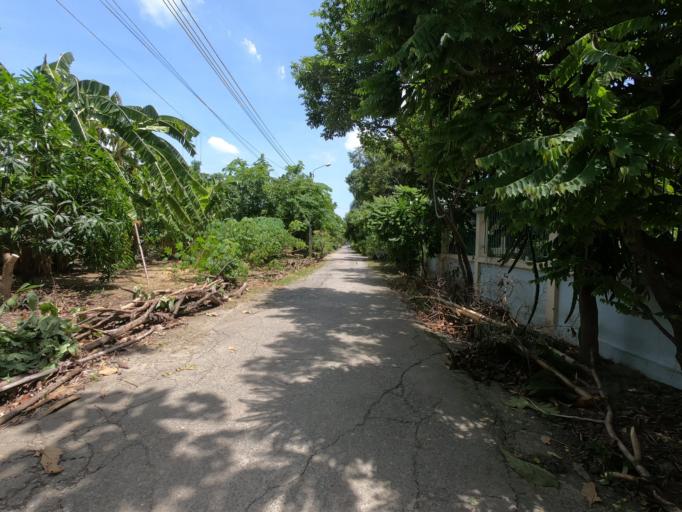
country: TH
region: Bangkok
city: Lat Phrao
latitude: 13.8257
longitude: 100.6253
